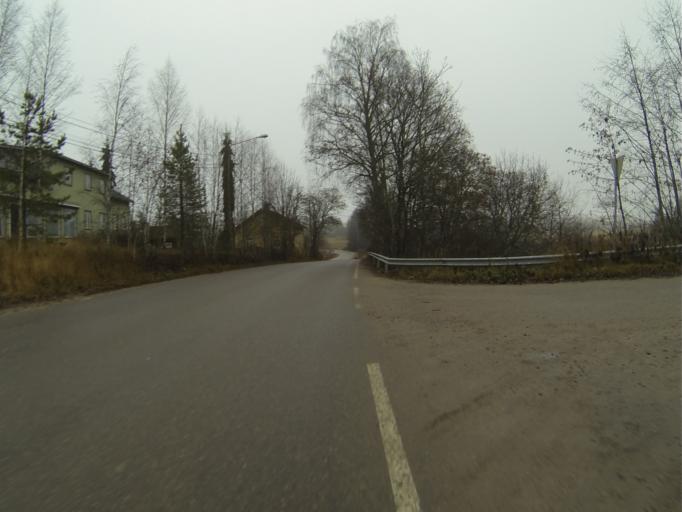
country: FI
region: Varsinais-Suomi
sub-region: Salo
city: Halikko
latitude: 60.4163
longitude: 22.9271
